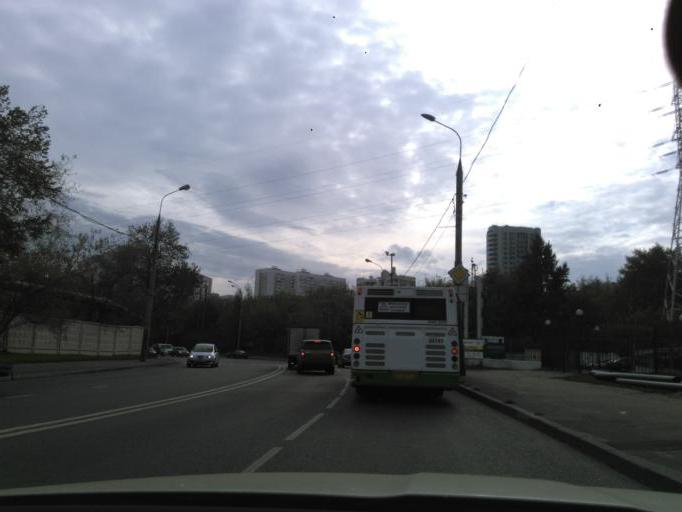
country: RU
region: Moscow
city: Mar'ina Roshcha
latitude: 55.8099
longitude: 37.6082
